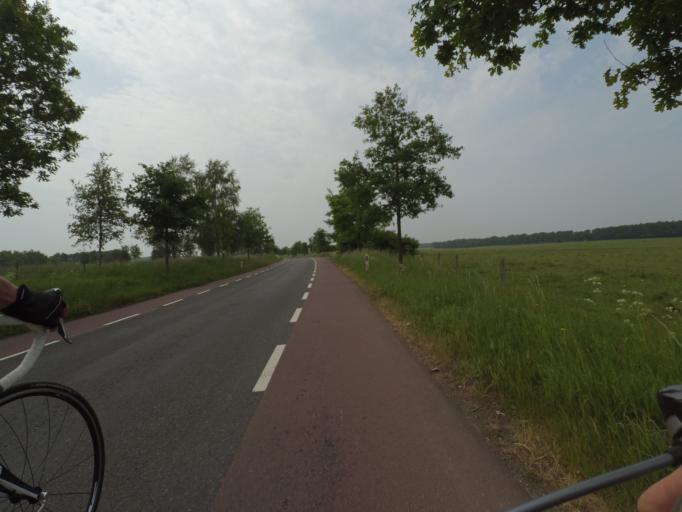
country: NL
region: Gelderland
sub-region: Gemeente Renkum
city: Heelsum
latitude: 52.0028
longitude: 5.7549
